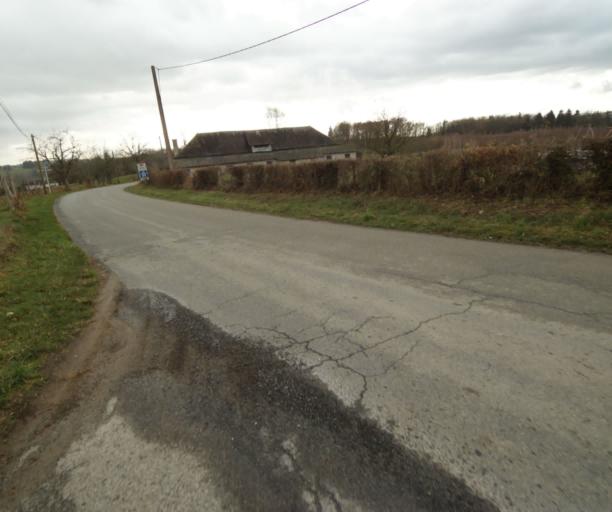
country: FR
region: Limousin
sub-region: Departement de la Correze
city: Saint-Mexant
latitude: 45.2816
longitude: 1.6212
